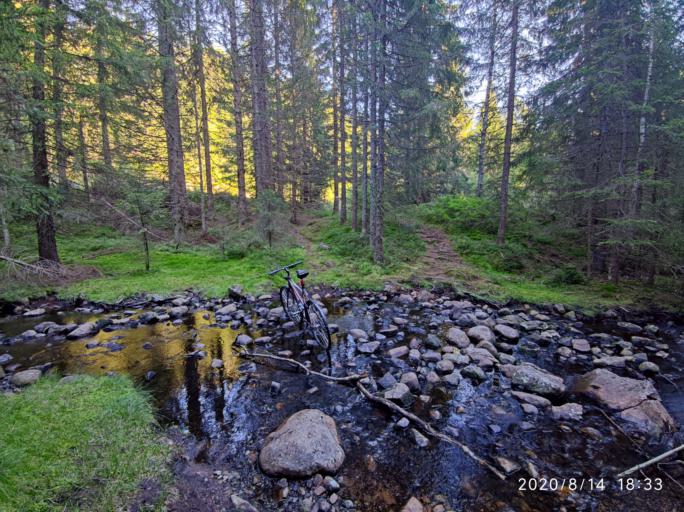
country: NO
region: Akershus
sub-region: Nannestad
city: Teigebyen
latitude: 60.1513
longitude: 10.9572
